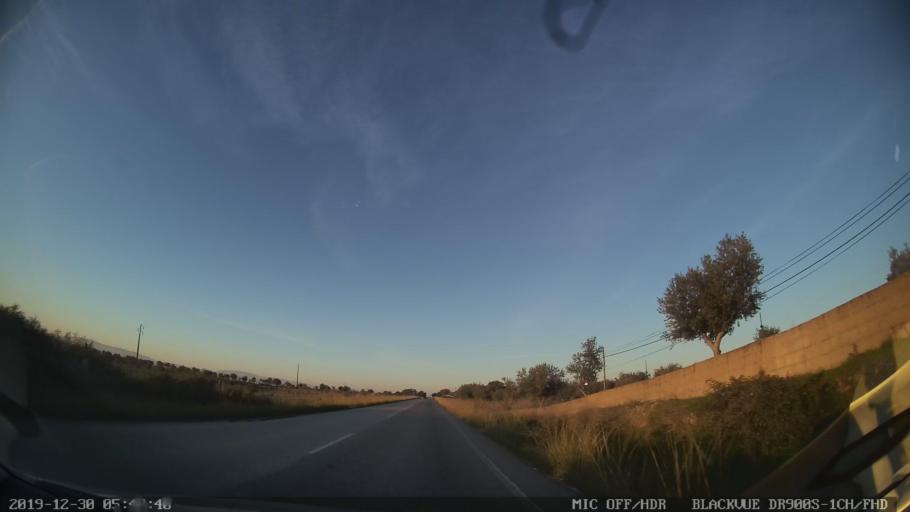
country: PT
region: Castelo Branco
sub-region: Idanha-A-Nova
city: Idanha-a-Nova
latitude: 39.9530
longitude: -7.2406
